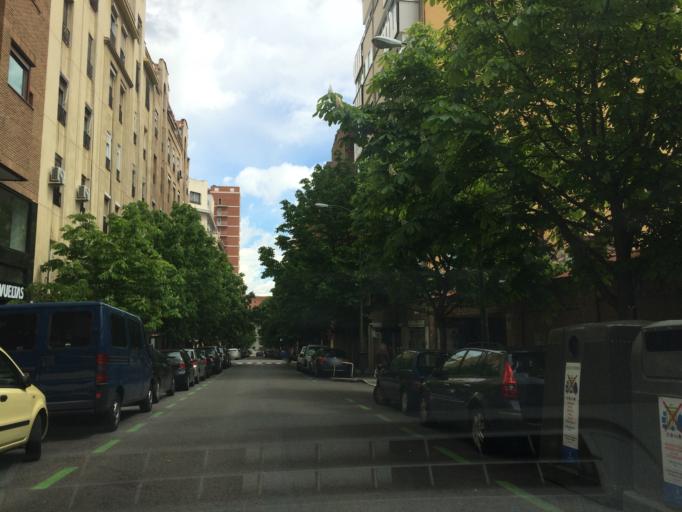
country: ES
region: Madrid
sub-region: Provincia de Madrid
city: Chamberi
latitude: 40.4430
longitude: -3.6983
